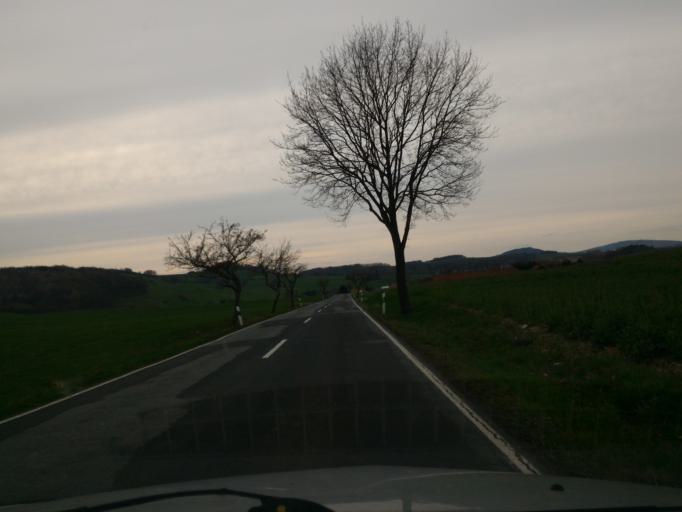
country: DE
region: Saxony
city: Mittelherwigsdorf
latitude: 50.9112
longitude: 14.7589
